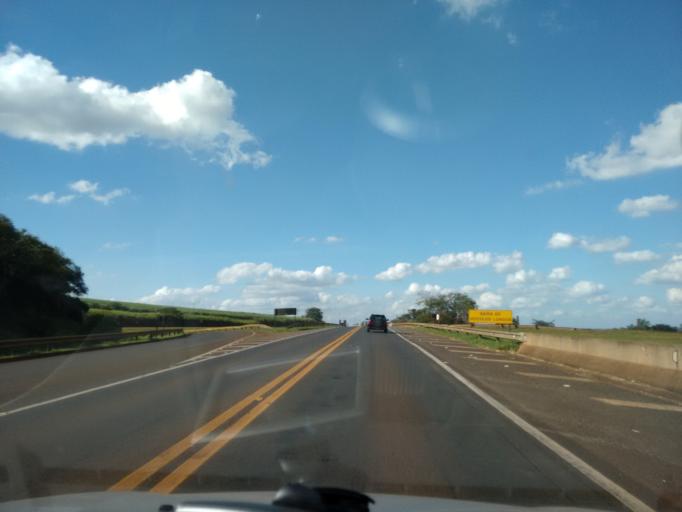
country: BR
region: Sao Paulo
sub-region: Americo Brasiliense
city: Americo Brasiliense
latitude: -21.7559
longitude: -48.0704
